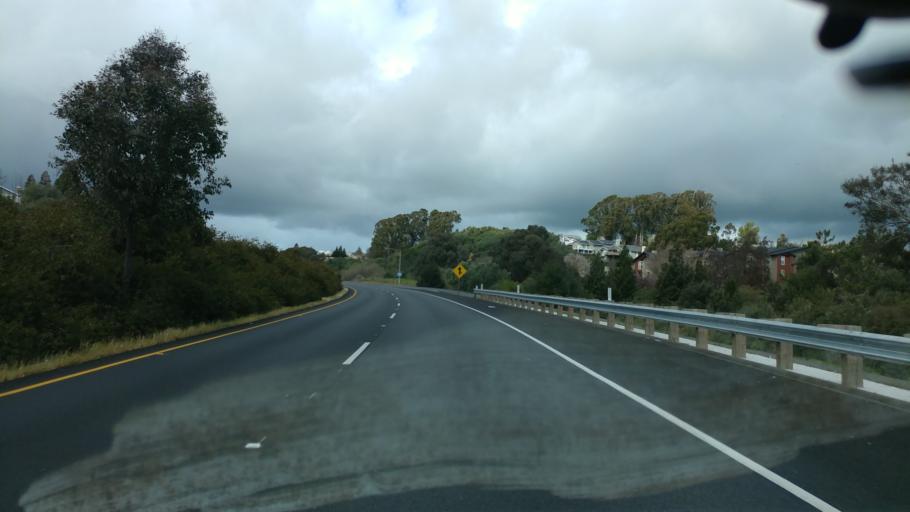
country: US
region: California
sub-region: Solano County
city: Benicia
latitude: 38.0597
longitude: -122.1510
